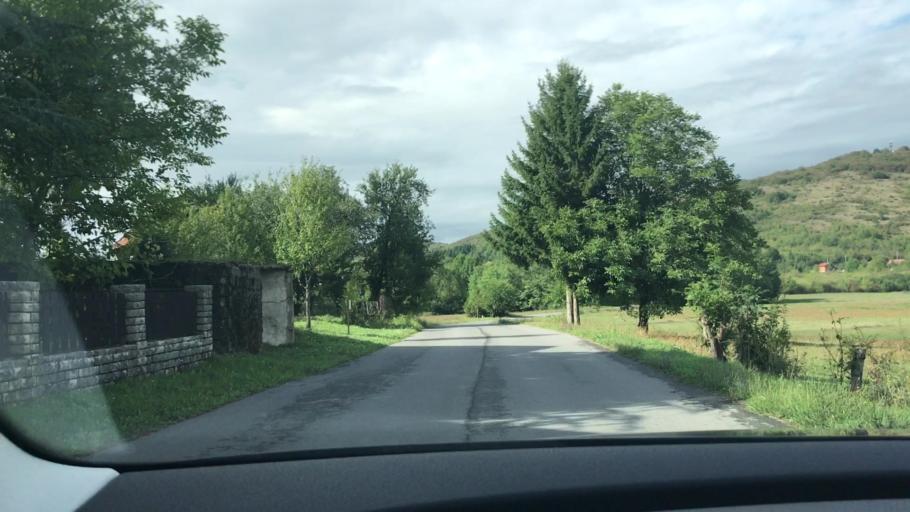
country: BA
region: Federation of Bosnia and Herzegovina
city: Izacic
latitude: 44.8724
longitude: 15.7176
